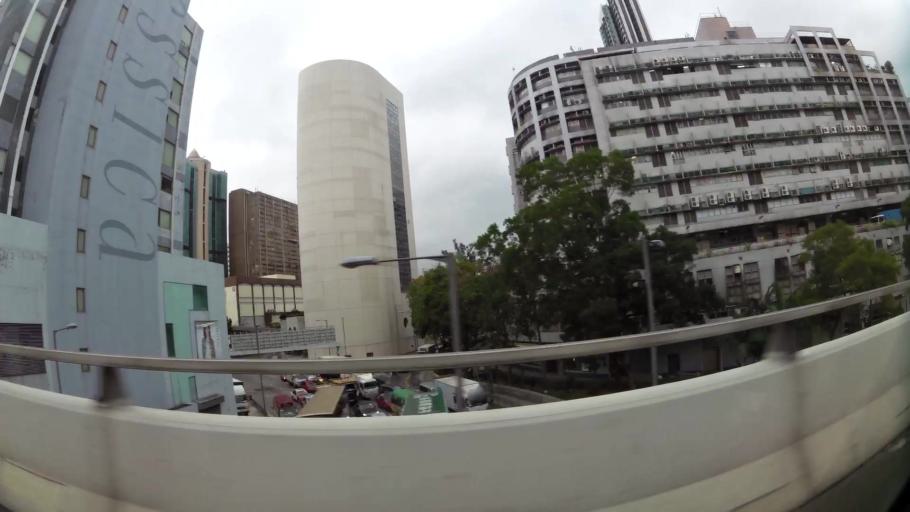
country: HK
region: Tsuen Wan
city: Tsuen Wan
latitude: 22.3701
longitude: 114.1343
